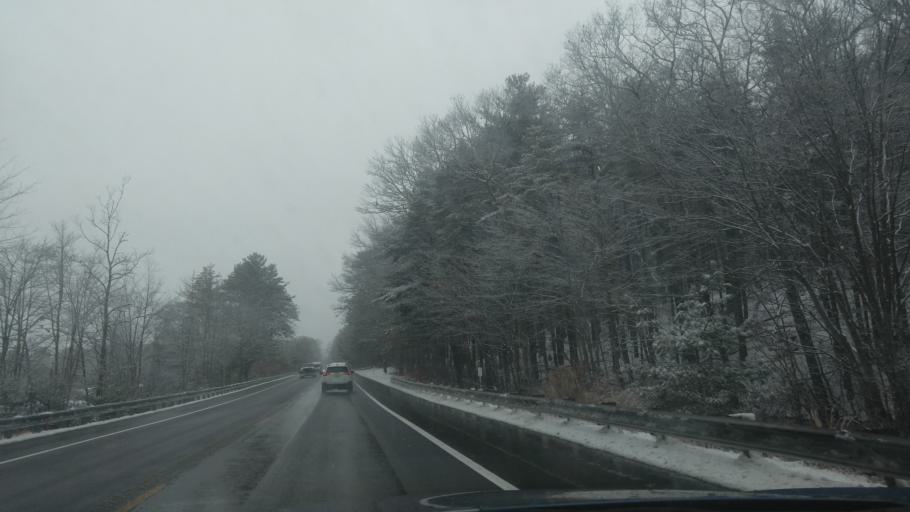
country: US
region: Rhode Island
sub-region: Providence County
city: North Scituate
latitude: 41.8384
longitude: -71.5895
